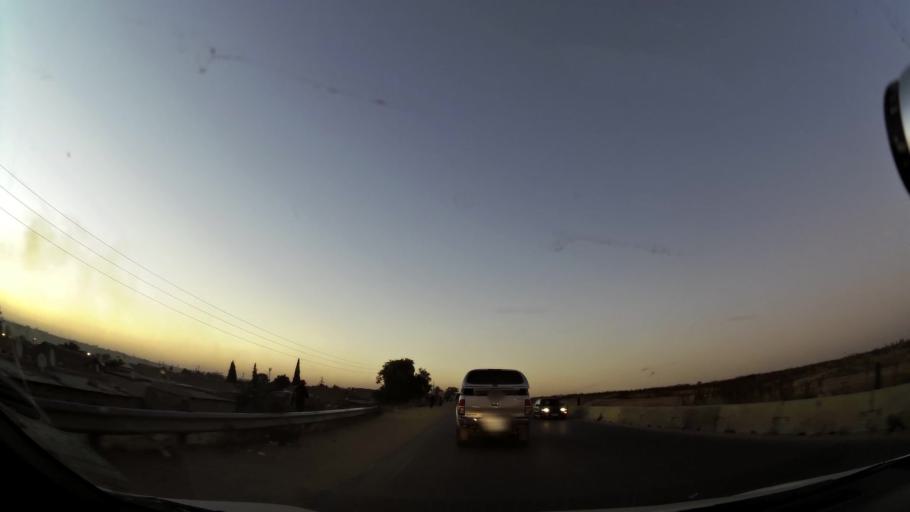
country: ZA
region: Gauteng
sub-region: City of Johannesburg Metropolitan Municipality
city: Diepsloot
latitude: -25.9345
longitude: 28.0211
